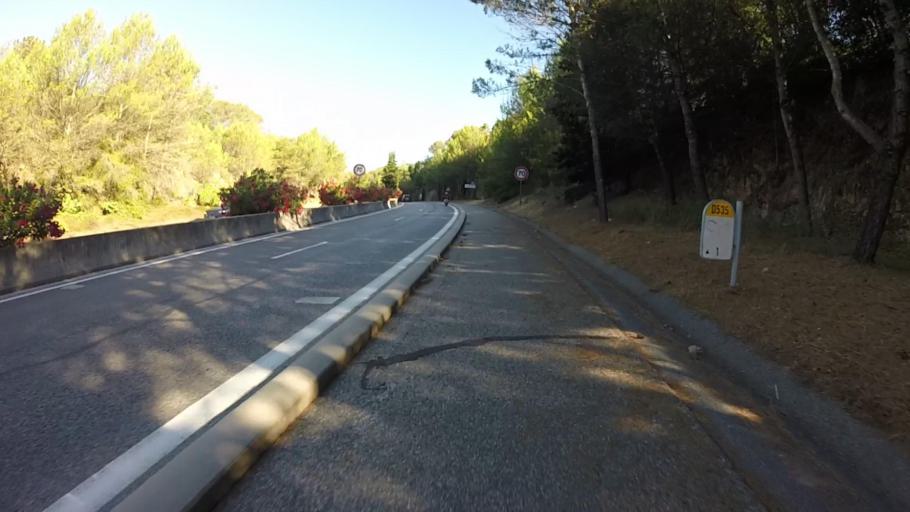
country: FR
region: Provence-Alpes-Cote d'Azur
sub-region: Departement des Alpes-Maritimes
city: Biot
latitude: 43.6106
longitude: 7.0817
